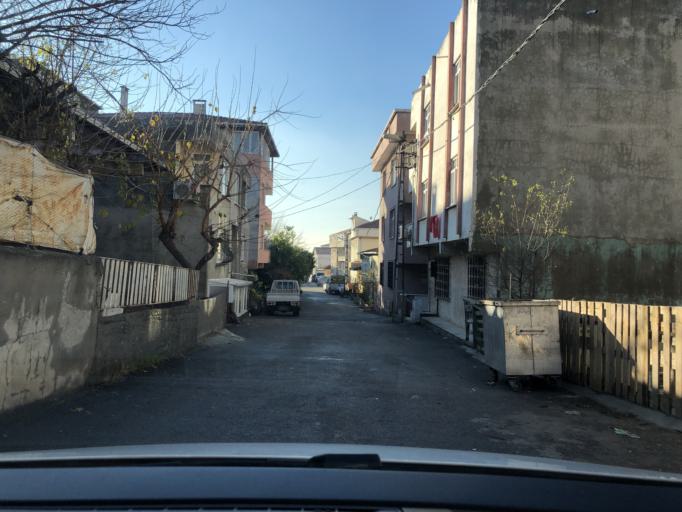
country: TR
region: Istanbul
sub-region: Atasehir
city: Atasehir
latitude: 40.9715
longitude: 29.1210
